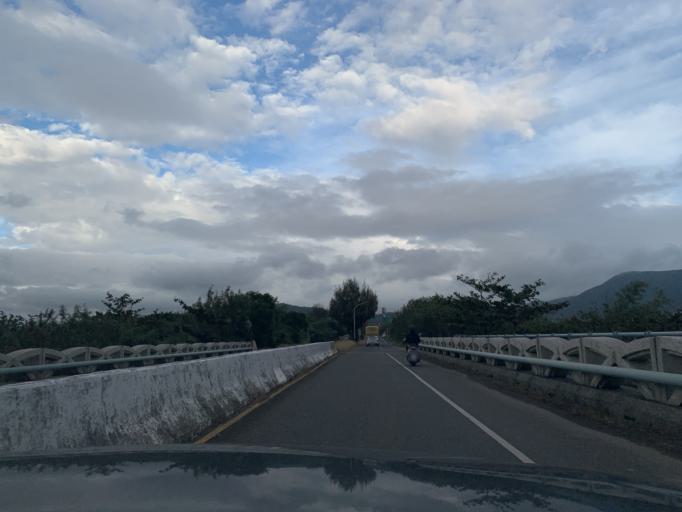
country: TW
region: Taiwan
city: Hengchun
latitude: 22.0524
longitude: 120.7194
